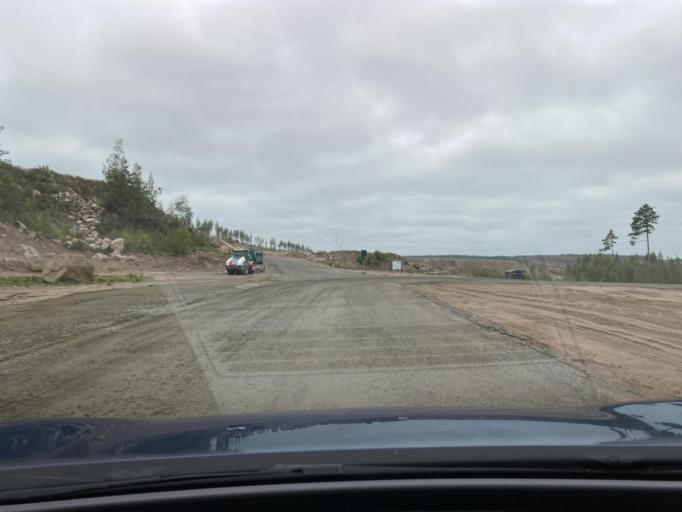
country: FI
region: Kymenlaakso
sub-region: Kouvola
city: Iitti
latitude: 60.8753
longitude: 26.4928
